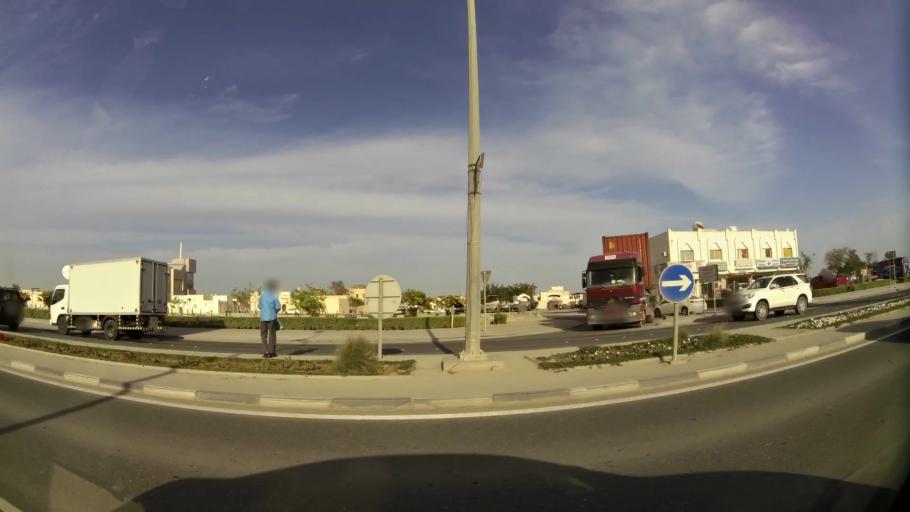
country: QA
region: Al Wakrah
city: Al Wakrah
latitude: 25.1676
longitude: 51.6076
